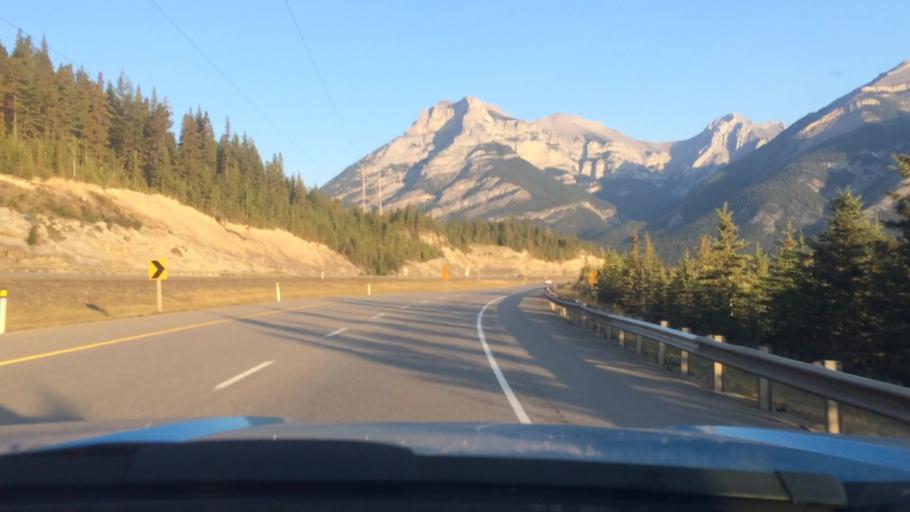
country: CA
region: Alberta
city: Canmore
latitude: 51.0480
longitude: -115.1838
